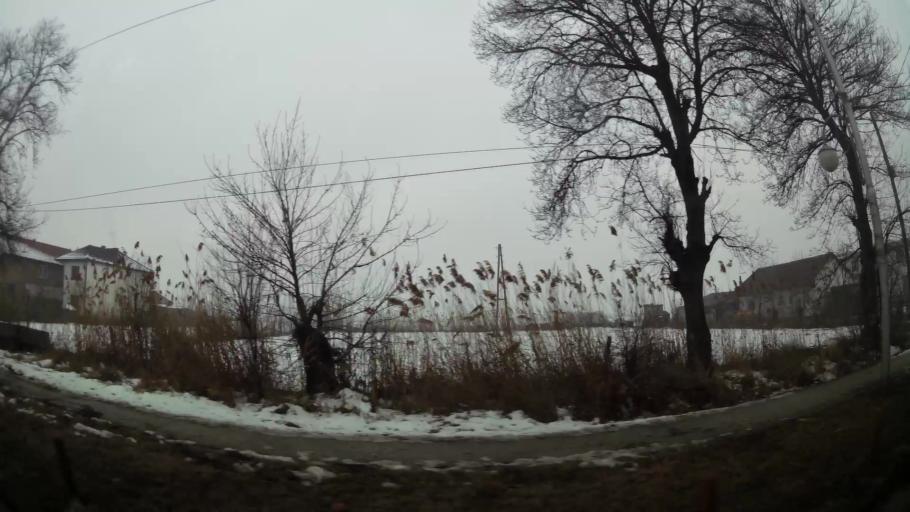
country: MK
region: Petrovec
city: Petrovec
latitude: 41.9305
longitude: 21.6254
